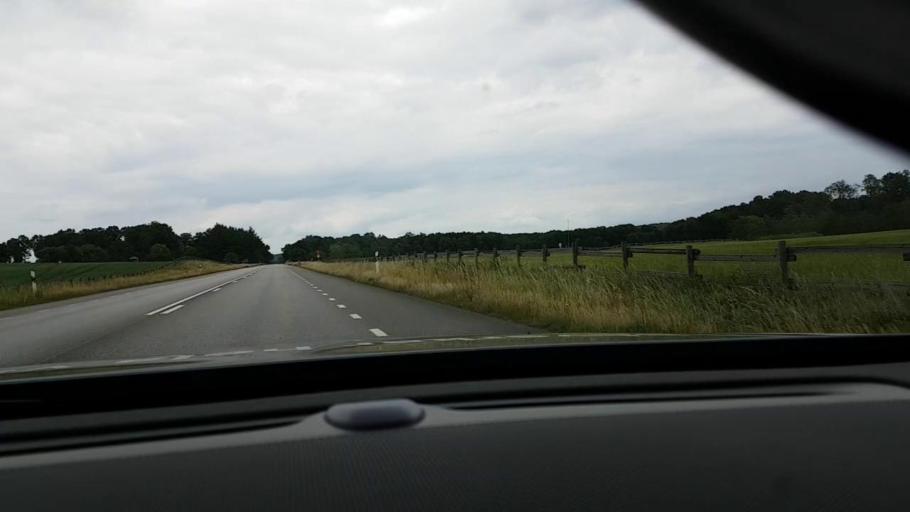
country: SE
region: Skane
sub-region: Hassleholms Kommun
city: Sosdala
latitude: 56.0520
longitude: 13.7195
